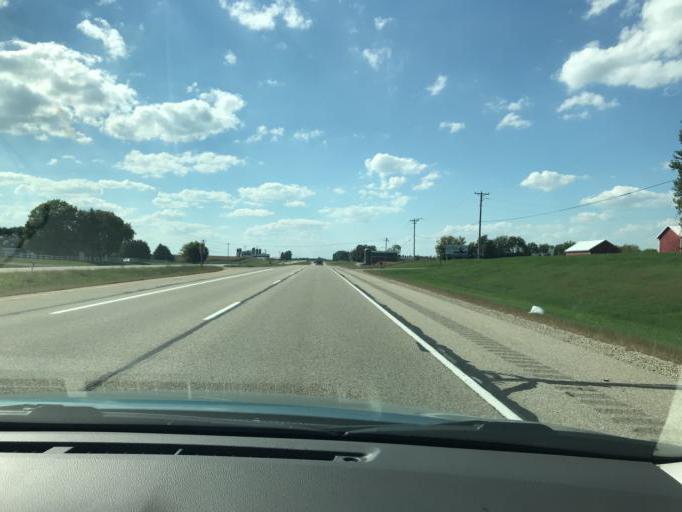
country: US
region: Wisconsin
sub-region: Kenosha County
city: Powers Lake
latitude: 42.5817
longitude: -88.3076
